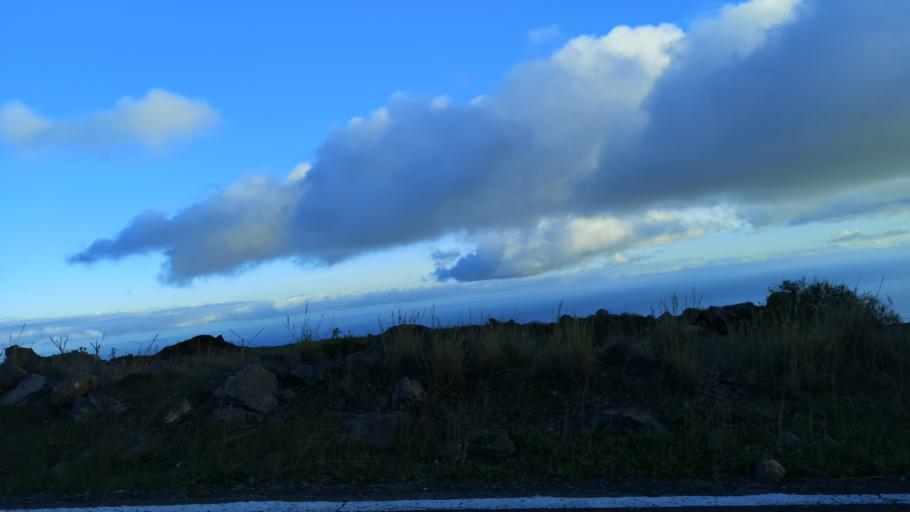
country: ES
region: Canary Islands
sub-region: Provincia de Santa Cruz de Tenerife
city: Alajero
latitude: 28.0513
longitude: -17.2330
